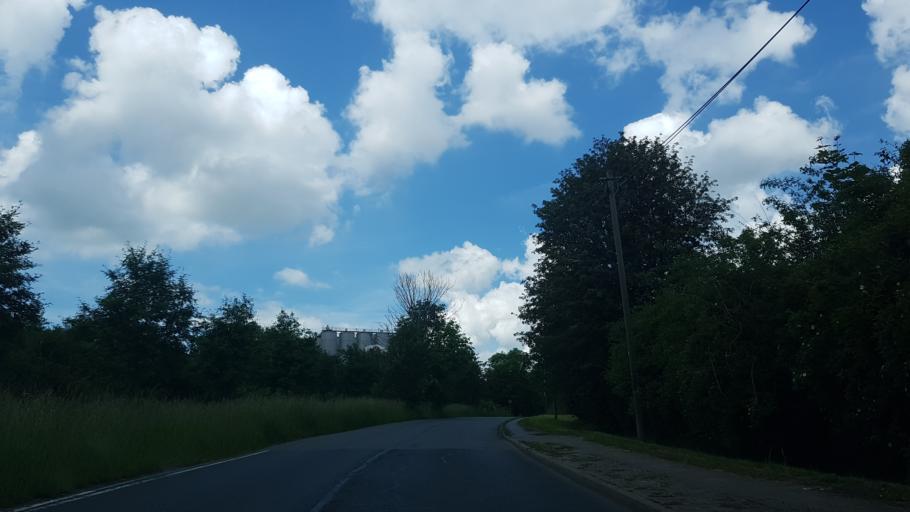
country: DE
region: Saxony
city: Bannewitz
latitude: 51.0151
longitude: 13.7149
